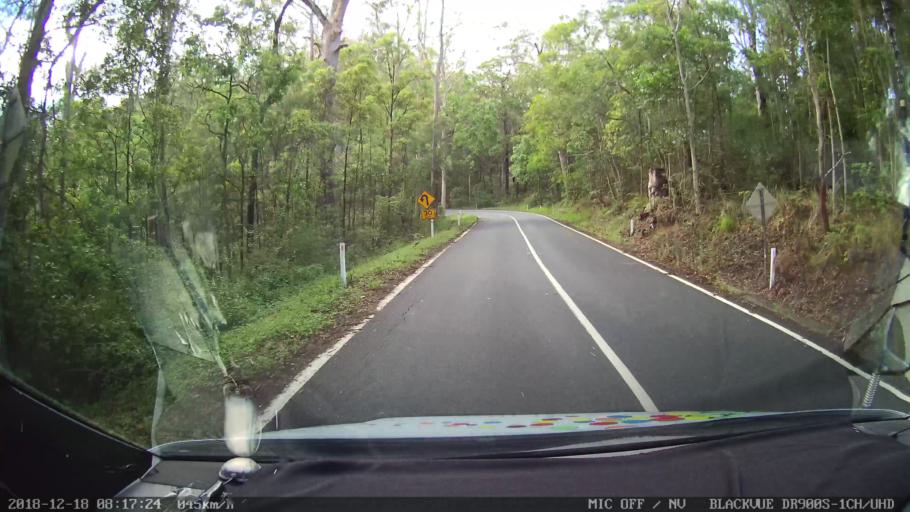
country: AU
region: New South Wales
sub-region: Kyogle
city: Kyogle
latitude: -28.3373
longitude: 152.7017
